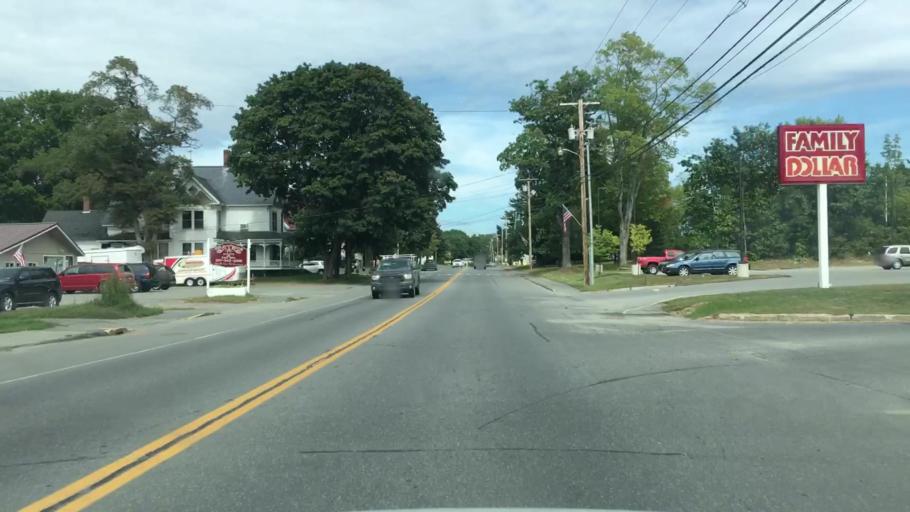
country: US
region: Maine
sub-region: Piscataquis County
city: Milo
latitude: 45.2562
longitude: -68.9870
